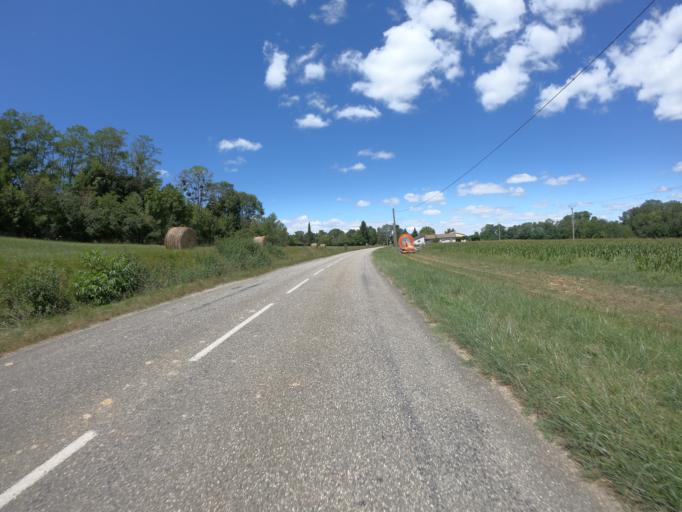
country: FR
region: Midi-Pyrenees
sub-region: Departement de l'Ariege
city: Verniolle
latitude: 43.0639
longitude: 1.7388
